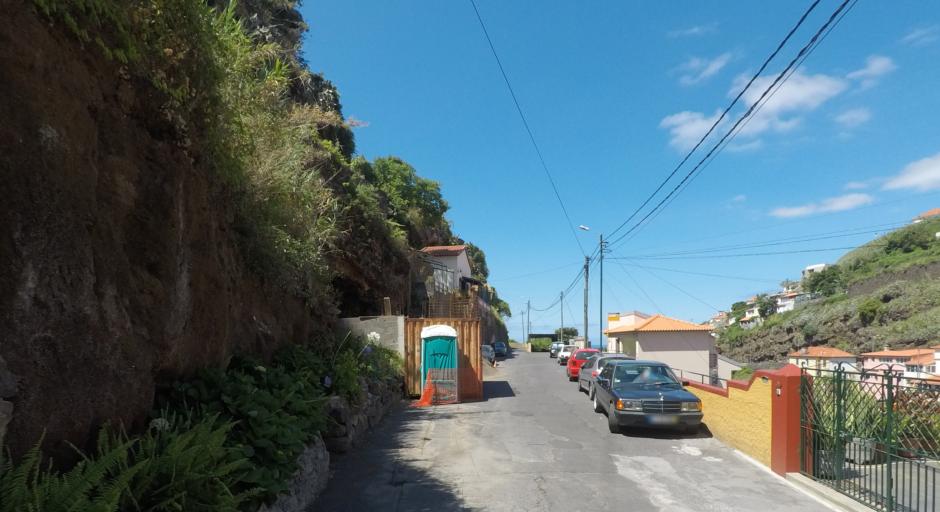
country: PT
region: Madeira
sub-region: Funchal
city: Funchal
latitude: 32.6493
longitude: -16.8855
